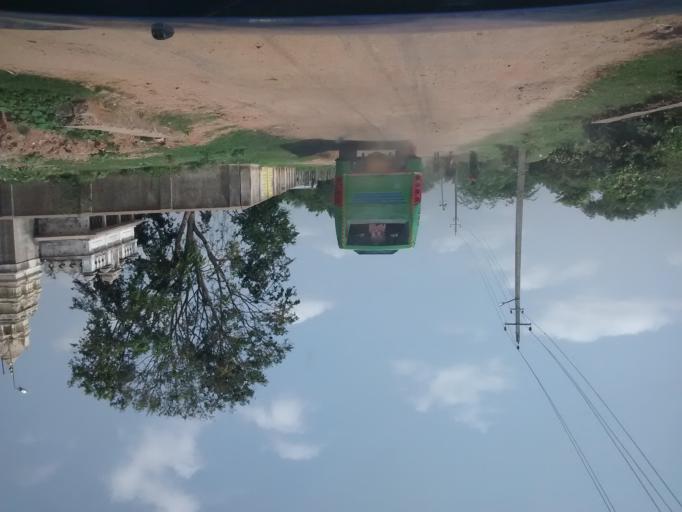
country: IN
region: Karnataka
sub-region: Hassan
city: Hole Narsipur
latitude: 12.6988
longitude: 76.1651
